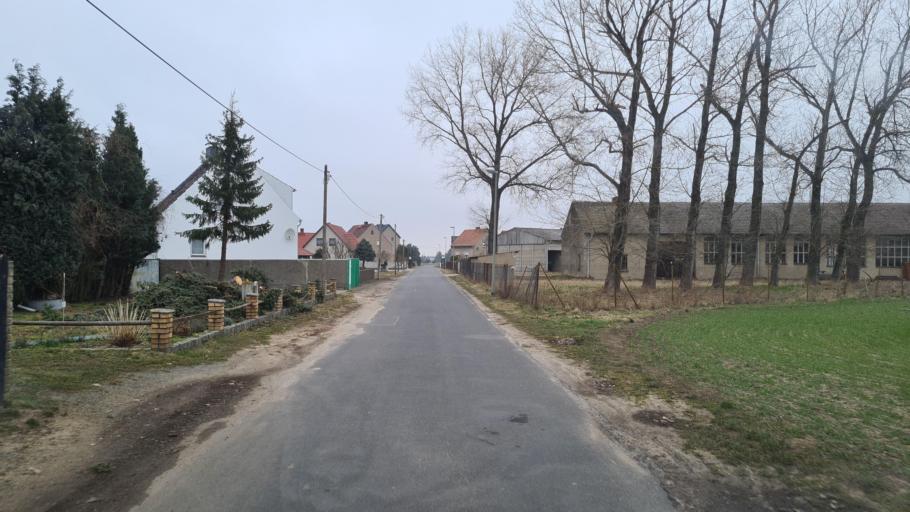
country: DE
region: Brandenburg
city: Herzberg
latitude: 51.6675
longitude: 13.1721
